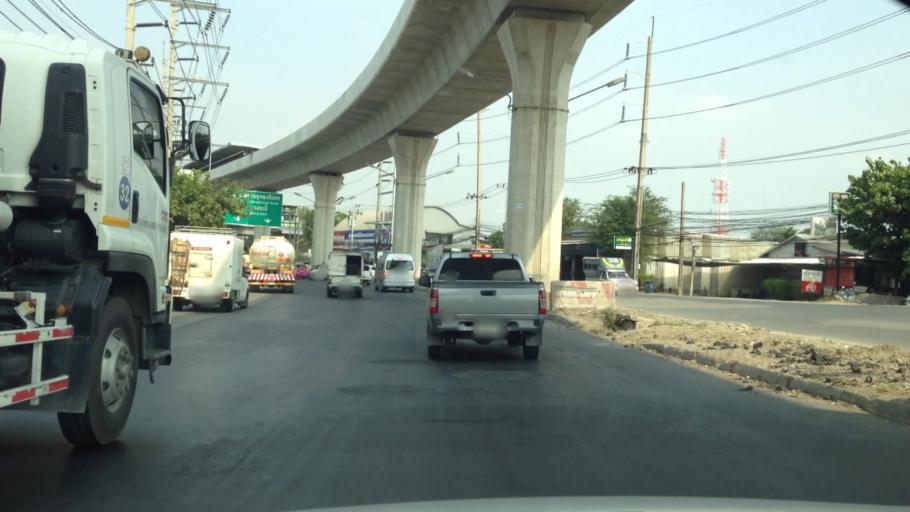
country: TH
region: Samut Prakan
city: Samut Prakan
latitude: 13.5900
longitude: 100.6097
